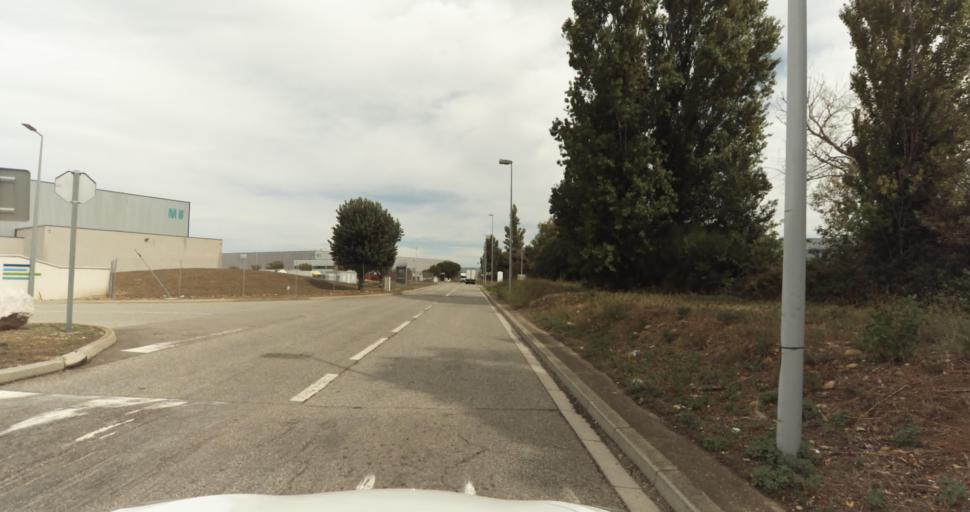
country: FR
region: Provence-Alpes-Cote d'Azur
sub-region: Departement des Bouches-du-Rhone
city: Miramas
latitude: 43.6059
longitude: 5.0000
